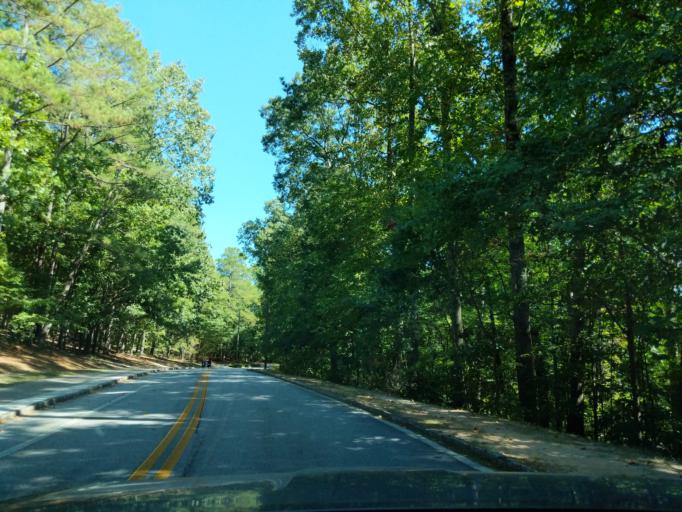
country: US
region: Georgia
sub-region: DeKalb County
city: Stone Mountain
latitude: 33.8035
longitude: -84.1565
